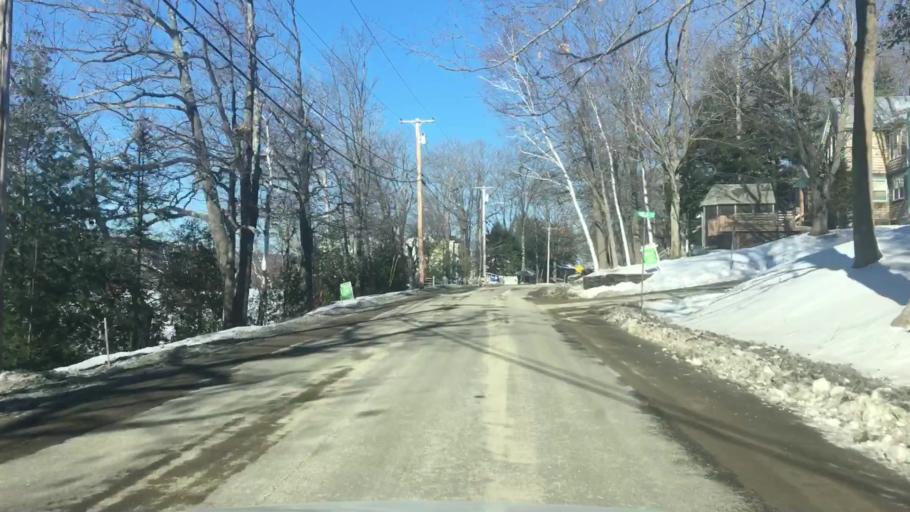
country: US
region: Maine
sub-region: Kennebec County
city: Winthrop
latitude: 44.3125
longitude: -69.9696
